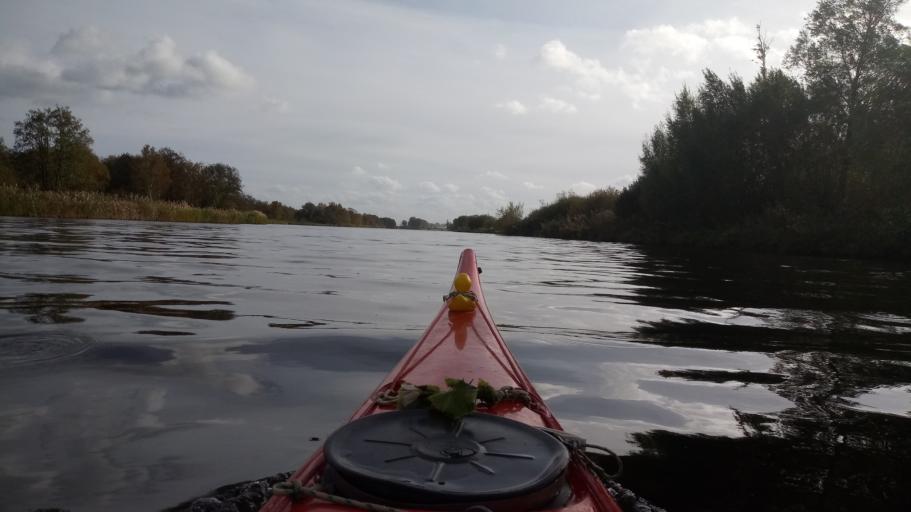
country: NL
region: Overijssel
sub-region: Gemeente Steenwijkerland
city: Wanneperveen
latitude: 52.6782
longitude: 6.0908
